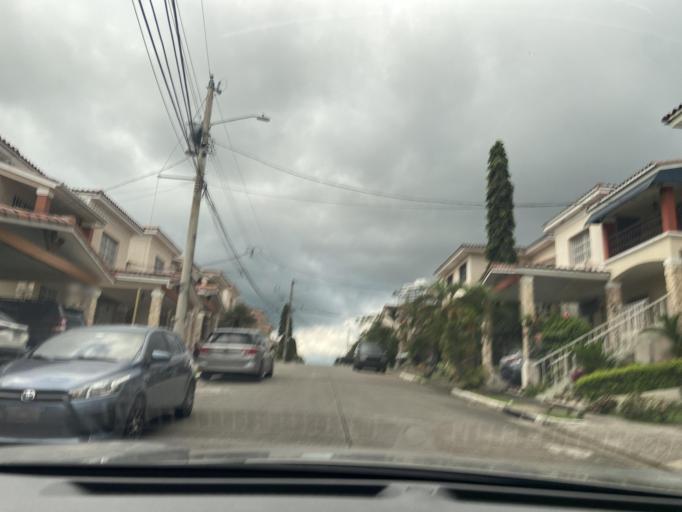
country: PA
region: Panama
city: Las Cumbres
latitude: 9.0432
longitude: -79.5205
